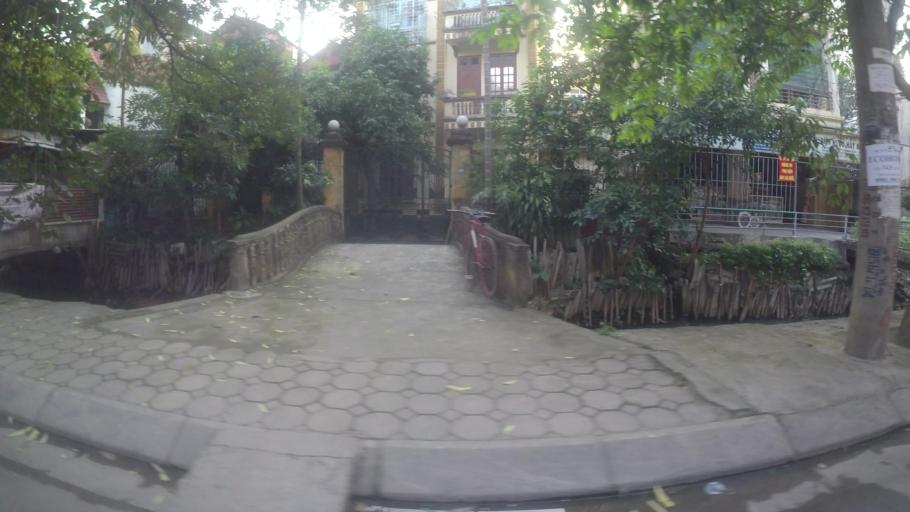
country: VN
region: Ha Noi
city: Tay Ho
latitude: 21.0689
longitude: 105.7915
